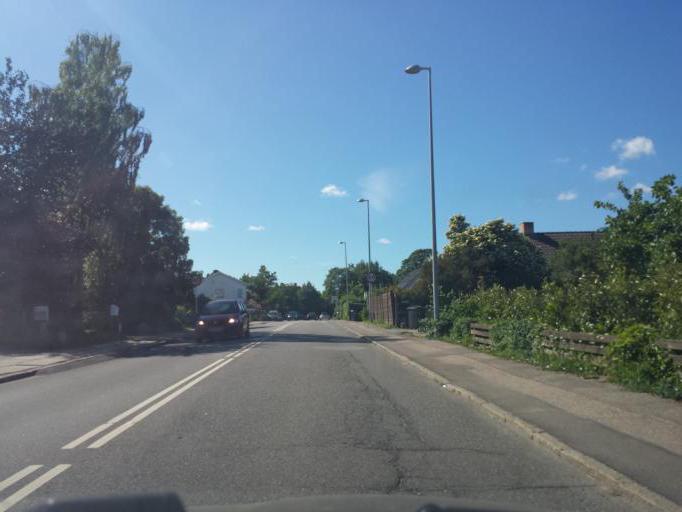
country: DK
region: Capital Region
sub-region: Egedal Kommune
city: Ganlose
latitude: 55.7896
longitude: 12.2659
